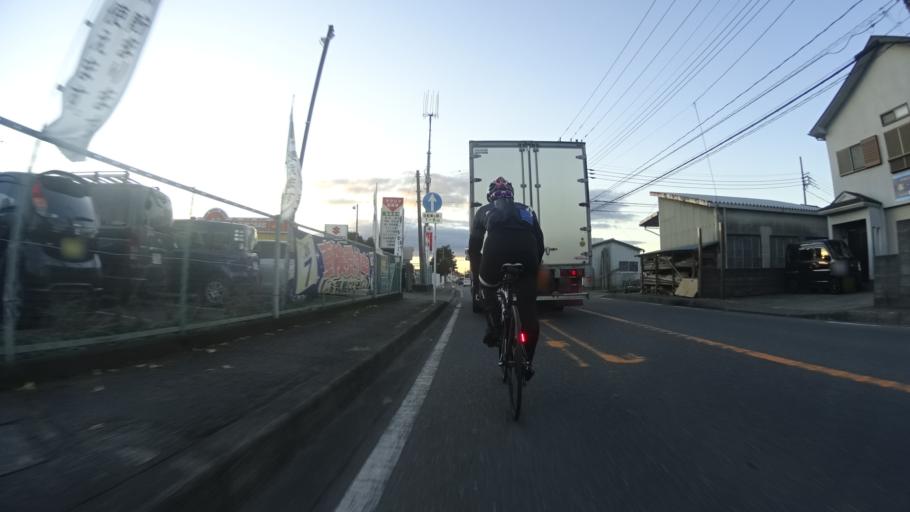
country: JP
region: Kanagawa
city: Zama
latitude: 35.5467
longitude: 139.3597
